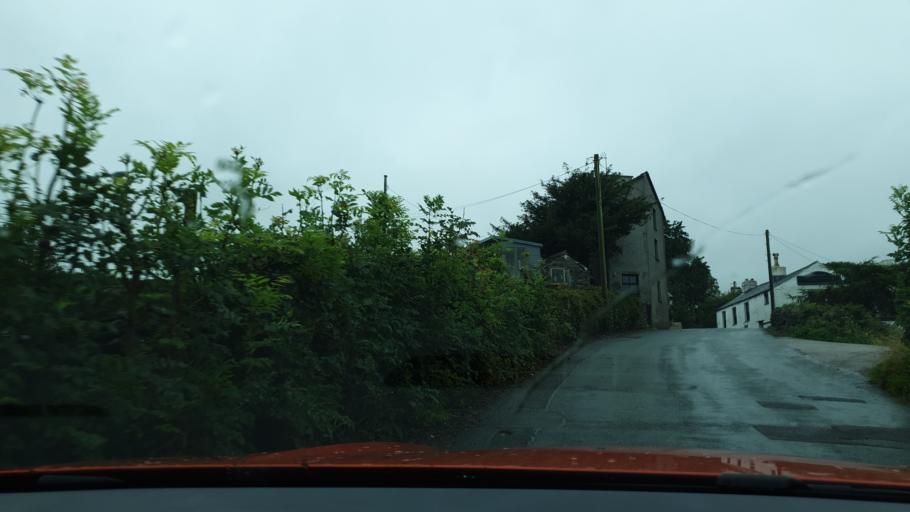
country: GB
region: England
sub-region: Cumbria
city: Ulverston
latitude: 54.2550
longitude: -3.0715
